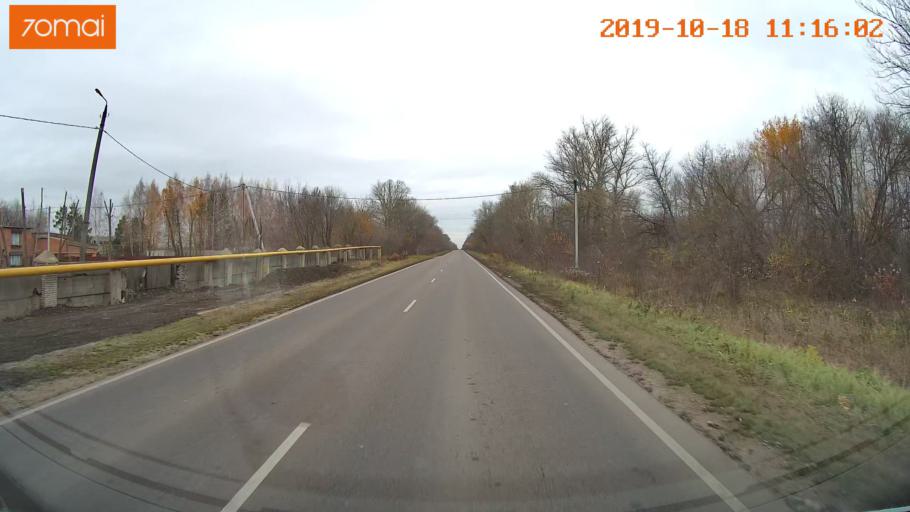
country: RU
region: Tula
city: Kimovsk
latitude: 54.0014
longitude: 38.5481
